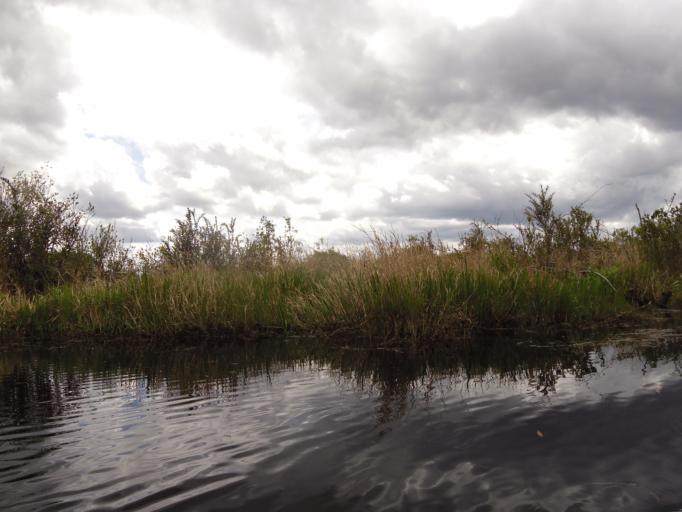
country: US
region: Georgia
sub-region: Charlton County
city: Folkston
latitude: 30.7368
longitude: -82.1670
